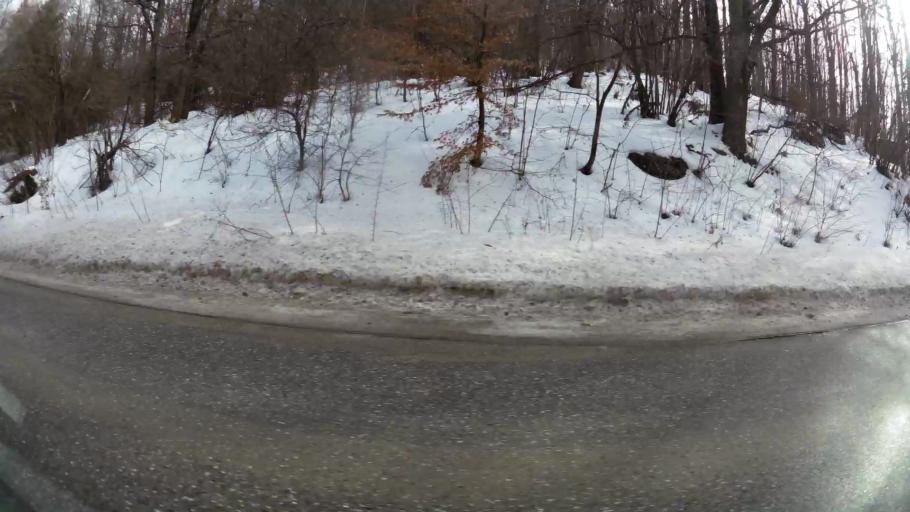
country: BG
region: Sofia-Capital
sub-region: Stolichna Obshtina
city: Sofia
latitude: 42.6353
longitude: 23.2254
